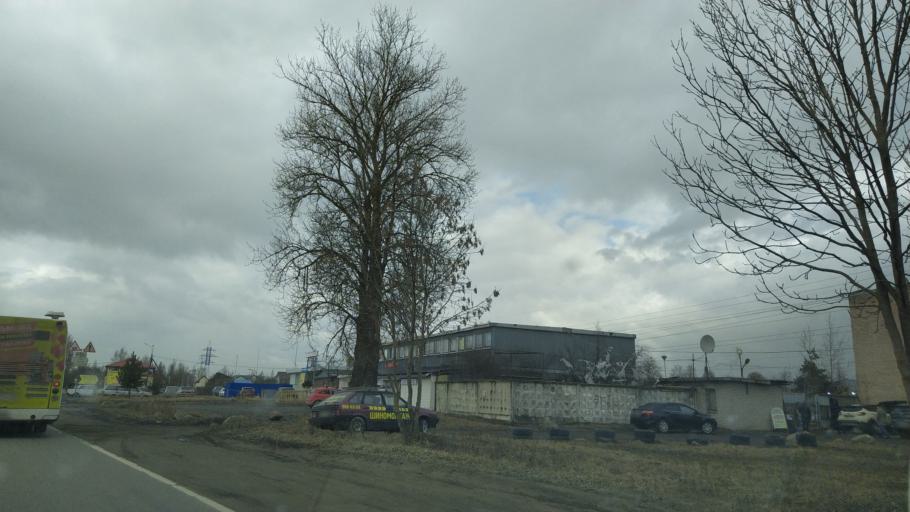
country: RU
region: St.-Petersburg
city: Tyarlevo
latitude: 59.7204
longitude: 30.4330
